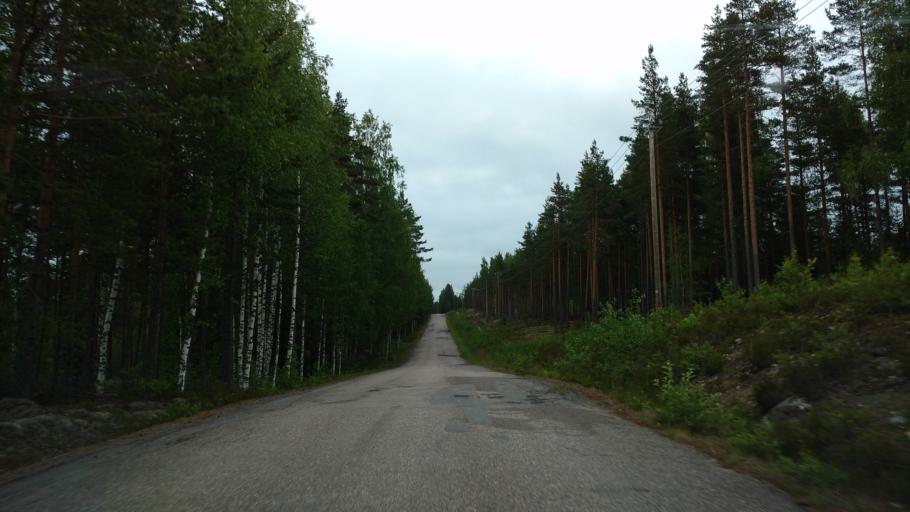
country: FI
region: Varsinais-Suomi
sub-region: Salo
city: Kiikala
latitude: 60.4691
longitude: 23.6492
